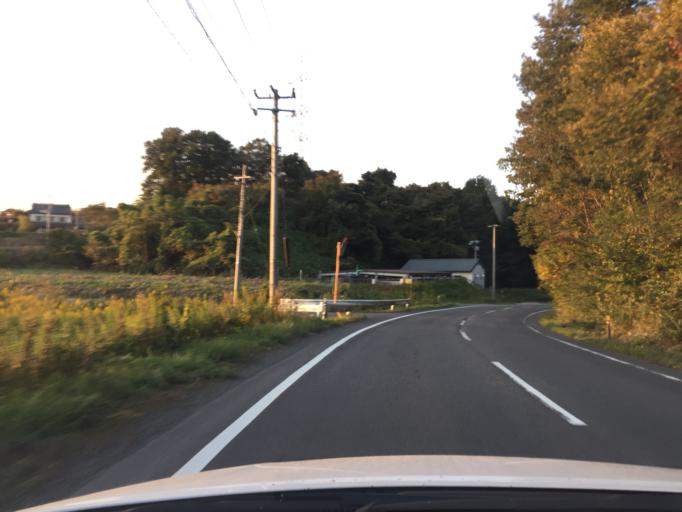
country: JP
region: Fukushima
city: Sukagawa
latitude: 37.3347
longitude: 140.4406
